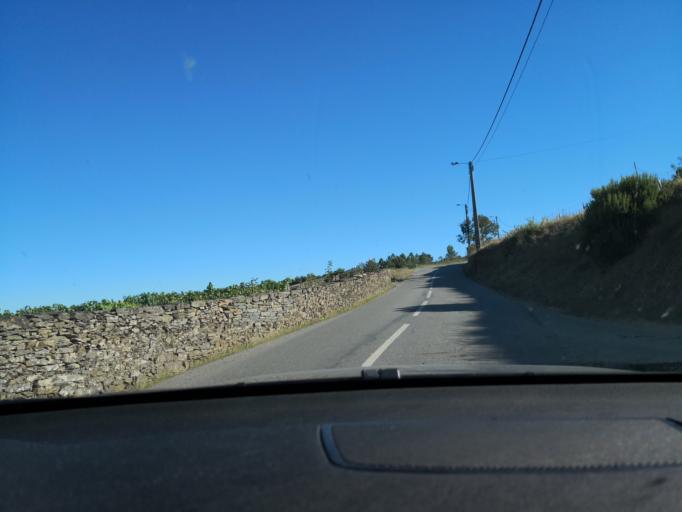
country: PT
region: Vila Real
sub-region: Sabrosa
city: Vilela
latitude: 41.2263
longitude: -7.5636
